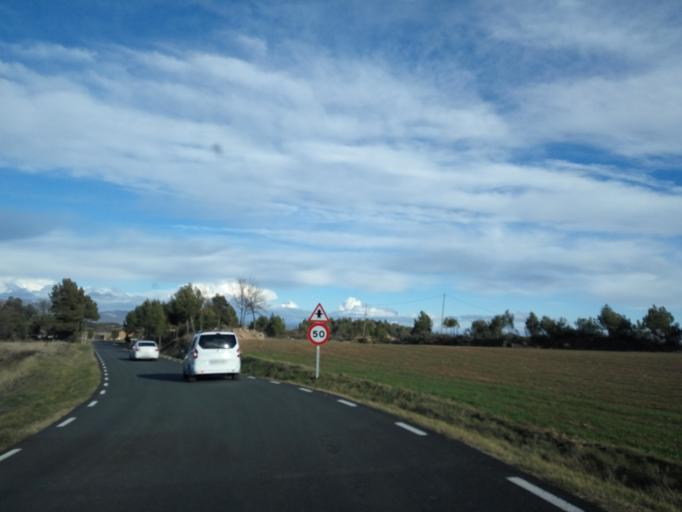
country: ES
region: Catalonia
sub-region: Provincia de Barcelona
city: Avia
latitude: 42.0233
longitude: 1.7994
